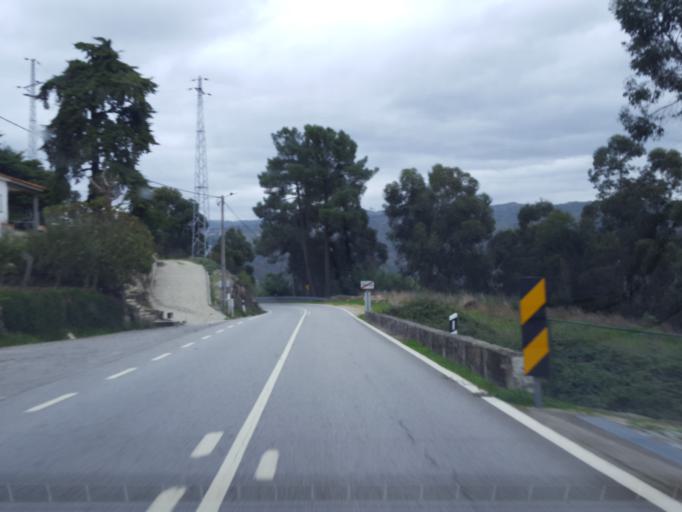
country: PT
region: Porto
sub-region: Marco de Canaveses
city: Marco de Canavezes
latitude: 41.1379
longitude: -8.1282
